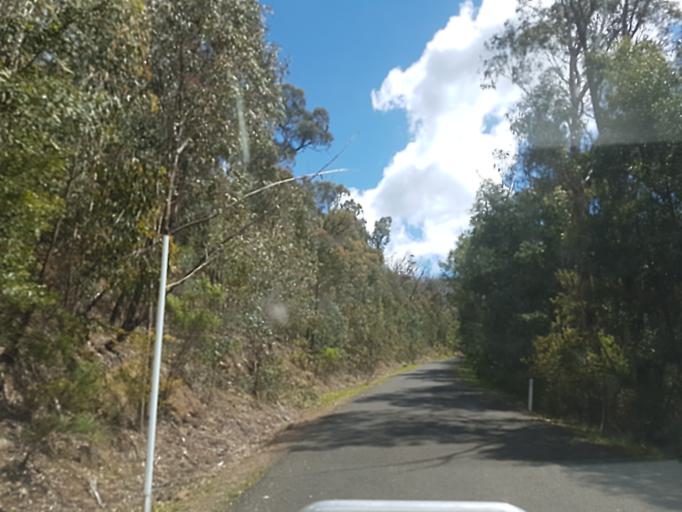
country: AU
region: Victoria
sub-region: East Gippsland
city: Bairnsdale
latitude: -37.4002
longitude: 147.2455
